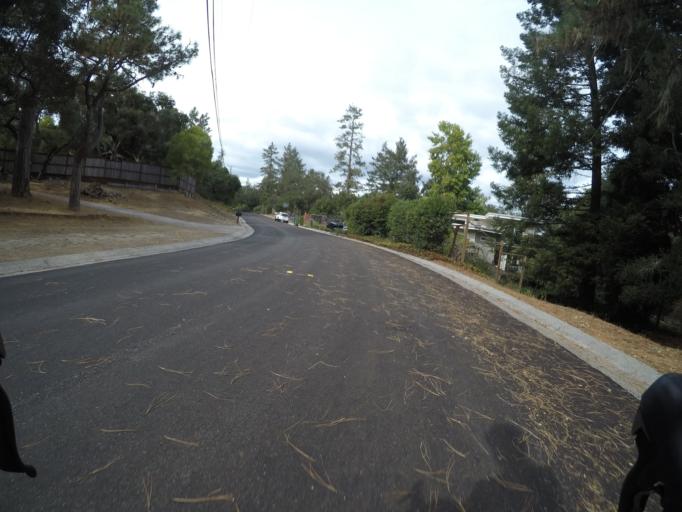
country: US
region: California
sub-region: Santa Cruz County
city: Mount Hermon
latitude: 37.0616
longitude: -122.0633
